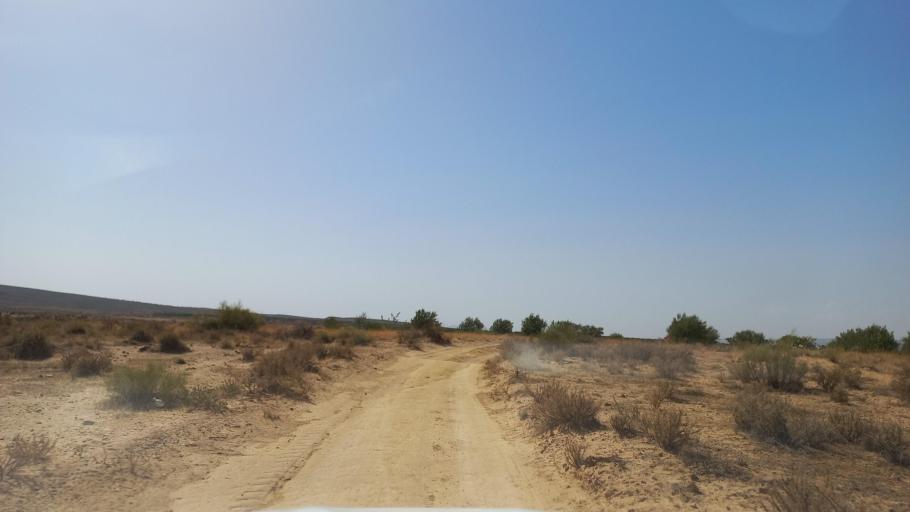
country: TN
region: Al Qasrayn
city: Kasserine
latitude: 35.2094
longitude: 9.0395
